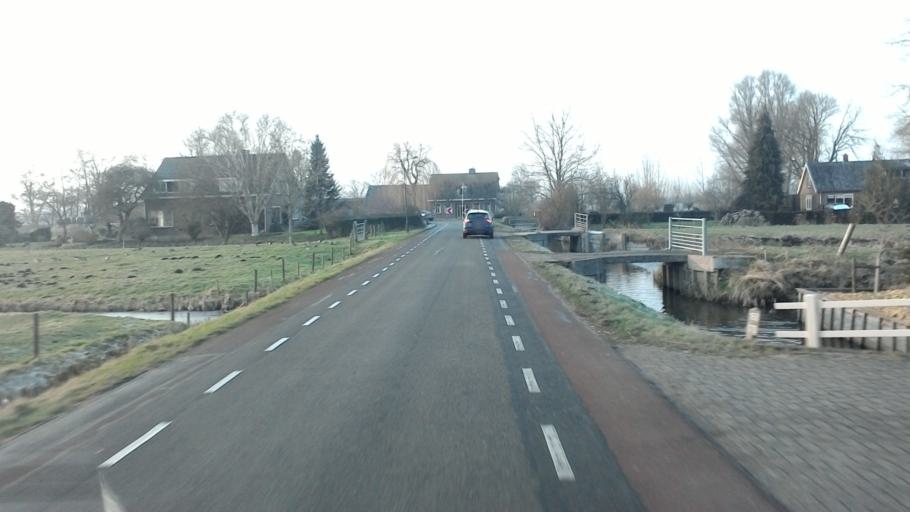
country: NL
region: North Holland
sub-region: Gemeente Wijdemeren
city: Oud-Loosdrecht
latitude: 52.1593
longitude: 5.1037
